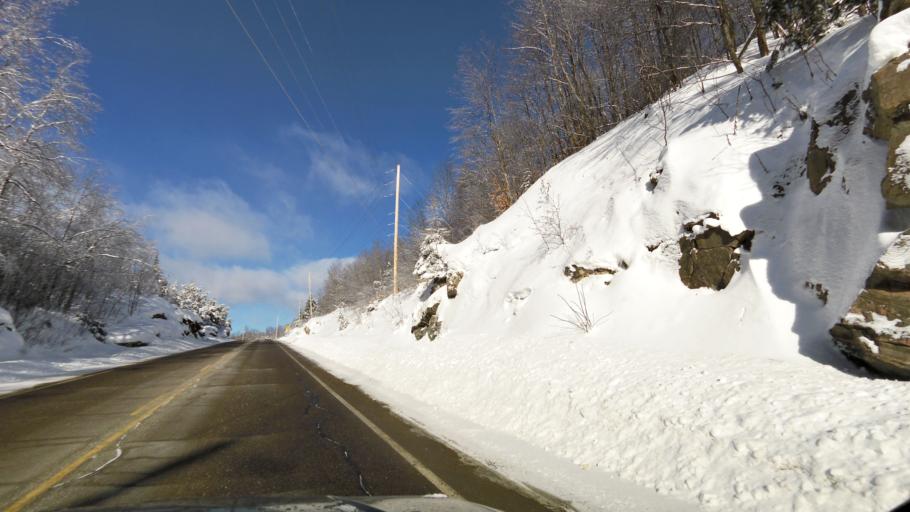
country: CA
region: Ontario
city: Bancroft
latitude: 44.9826
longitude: -78.2820
